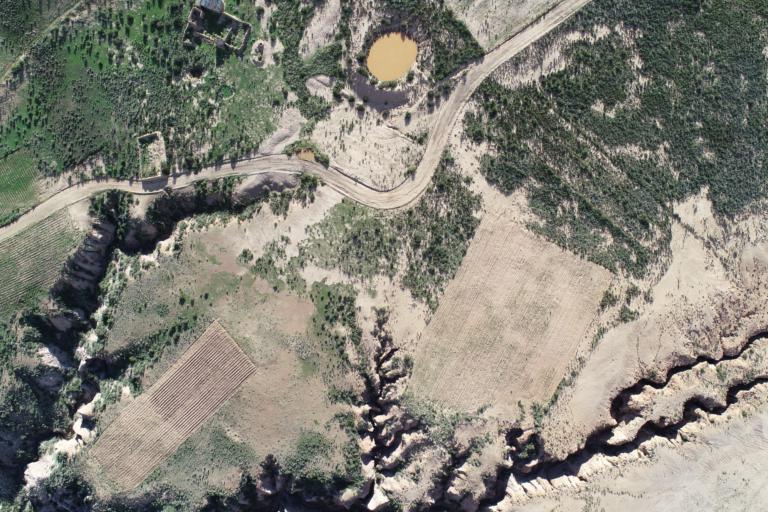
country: BO
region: La Paz
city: Curahuara de Carangas
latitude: -17.2973
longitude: -68.4912
